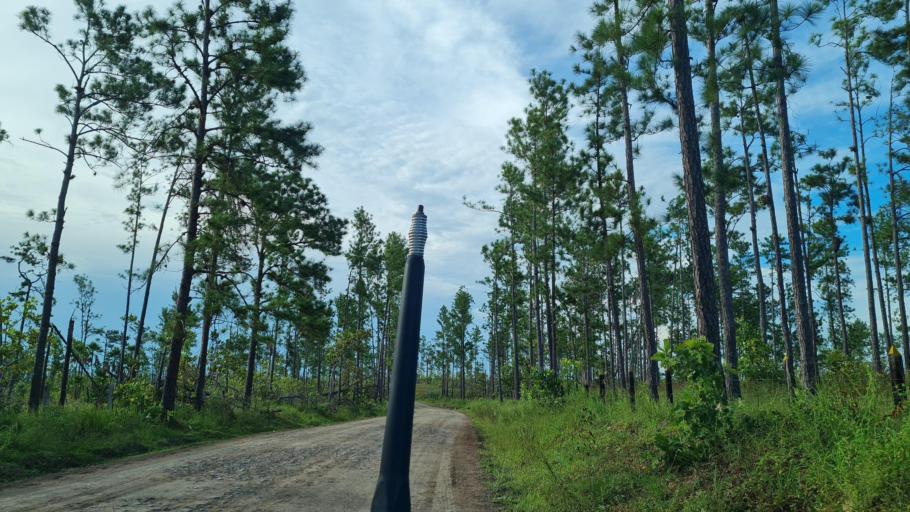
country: NI
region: Atlantico Sur
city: La Cruz de Rio Grande
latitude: 13.5603
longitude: -84.3044
